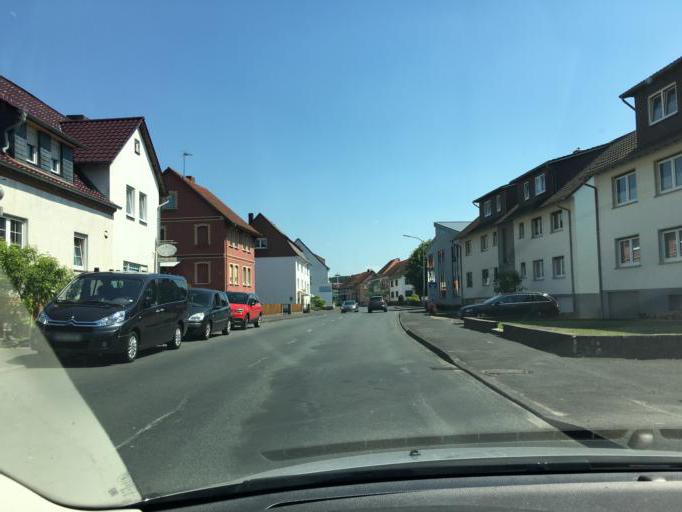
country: DE
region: Hesse
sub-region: Regierungsbezirk Kassel
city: Ronshausen
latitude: 50.9493
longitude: 9.8549
